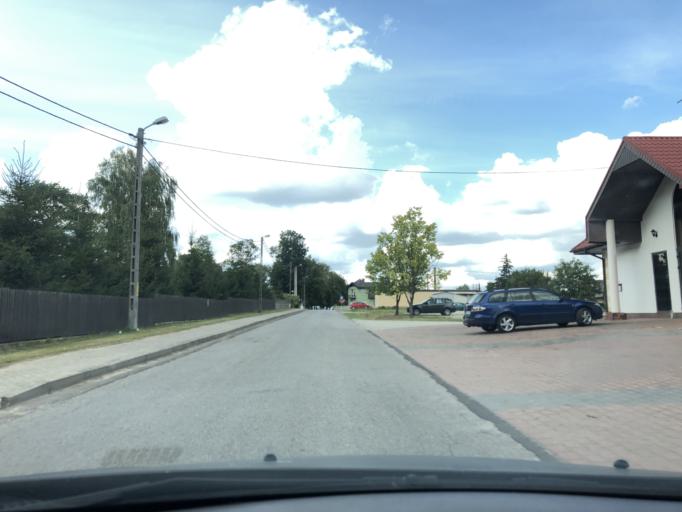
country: PL
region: Lodz Voivodeship
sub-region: Powiat wieruszowski
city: Walichnowy
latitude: 51.2603
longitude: 18.3941
